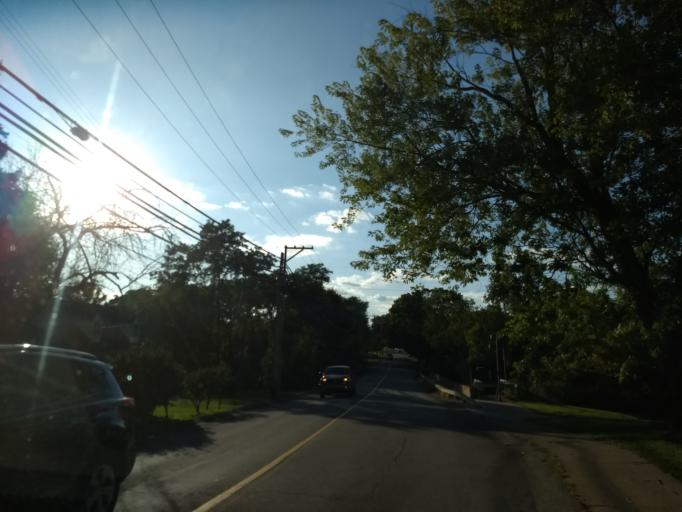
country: US
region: Pennsylvania
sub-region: Allegheny County
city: Mount Lebanon
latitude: 40.3481
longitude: -80.0392
